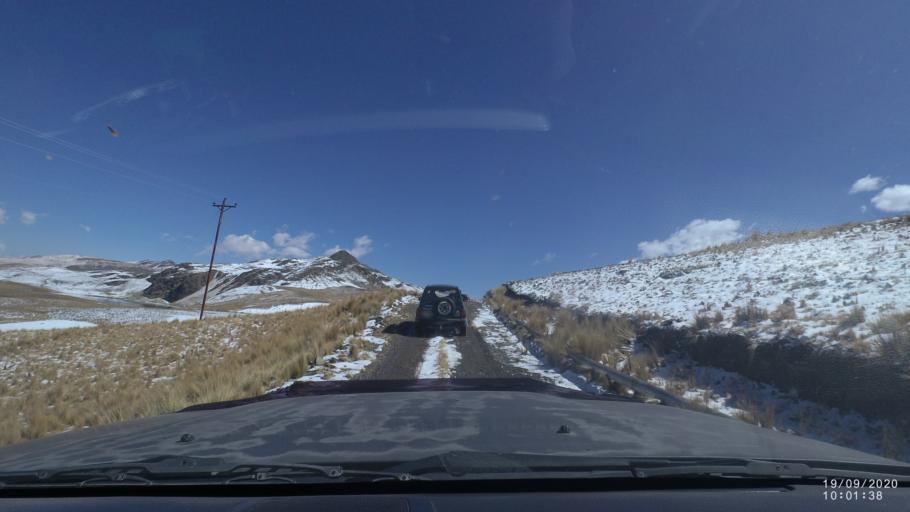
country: BO
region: Cochabamba
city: Cochabamba
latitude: -17.3014
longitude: -66.0916
